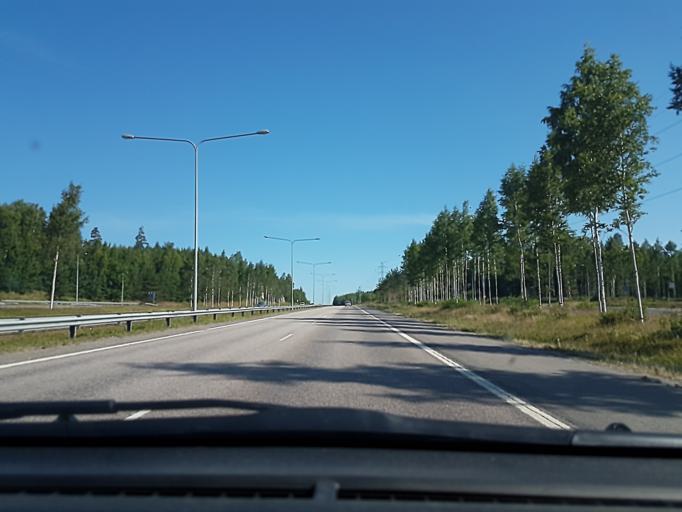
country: FI
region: Uusimaa
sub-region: Helsinki
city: Vantaa
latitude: 60.3238
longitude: 24.9977
